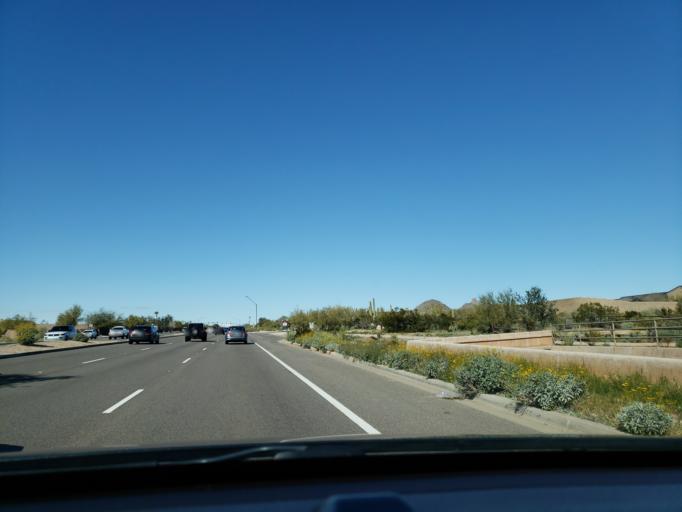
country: US
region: Arizona
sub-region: Maricopa County
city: Carefree
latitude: 33.6831
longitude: -111.8905
